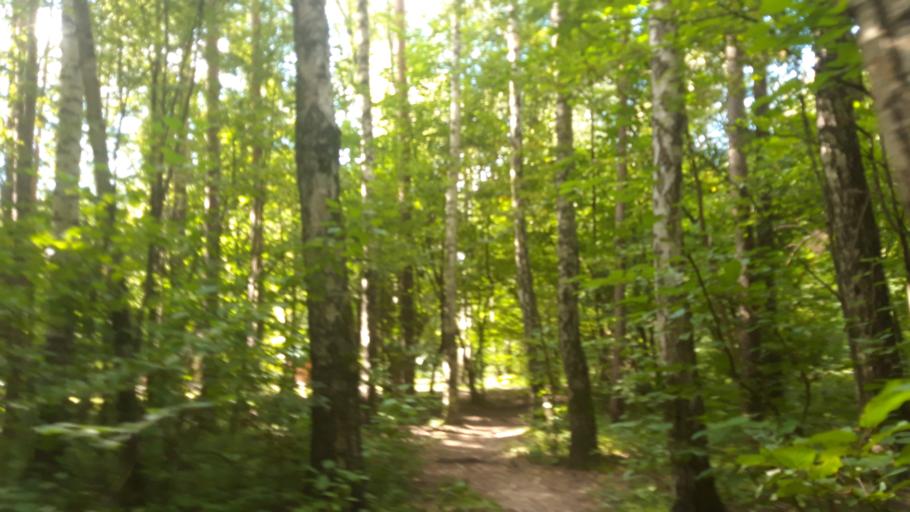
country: RU
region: Moscow
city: Zelenograd
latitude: 55.9920
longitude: 37.1995
